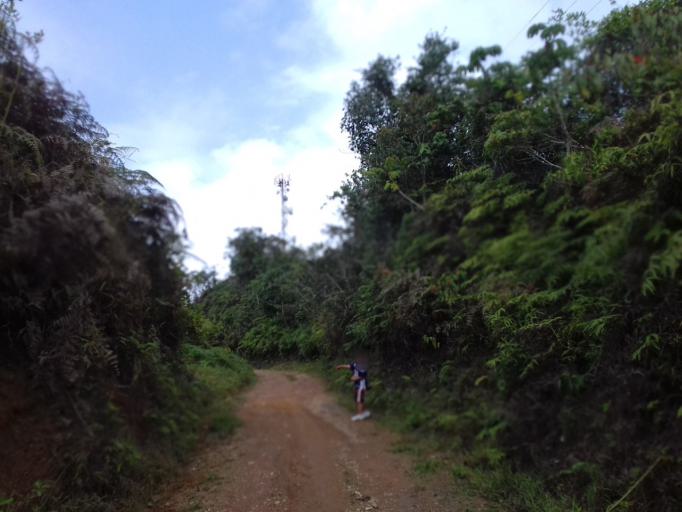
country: CO
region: Tolima
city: Libano
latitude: 4.9354
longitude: -75.0489
